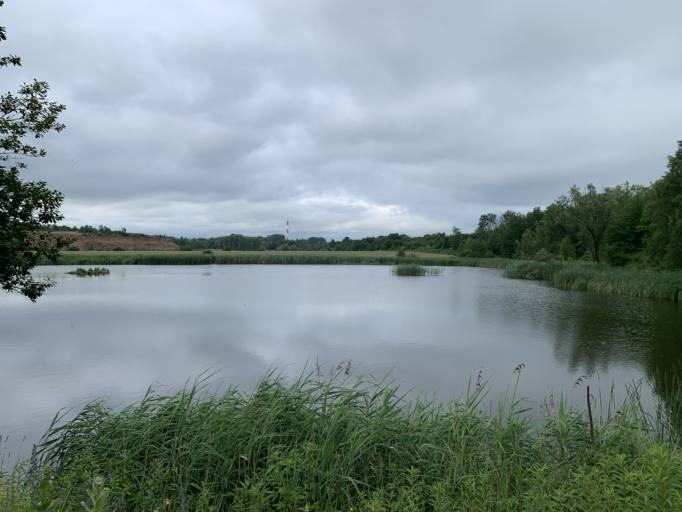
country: PL
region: Silesian Voivodeship
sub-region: Bytom
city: Bytom
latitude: 50.3312
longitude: 18.9532
